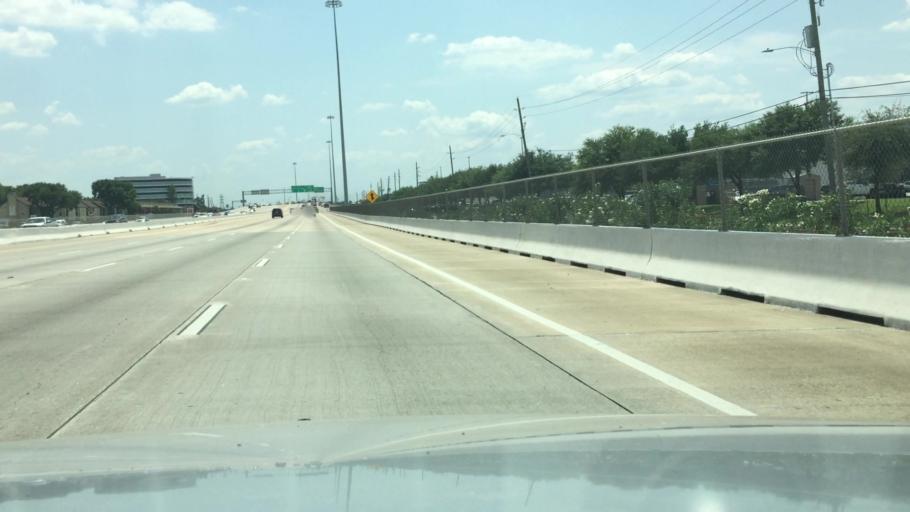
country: US
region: Texas
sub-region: Fort Bend County
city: Meadows Place
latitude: 29.6811
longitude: -95.5593
